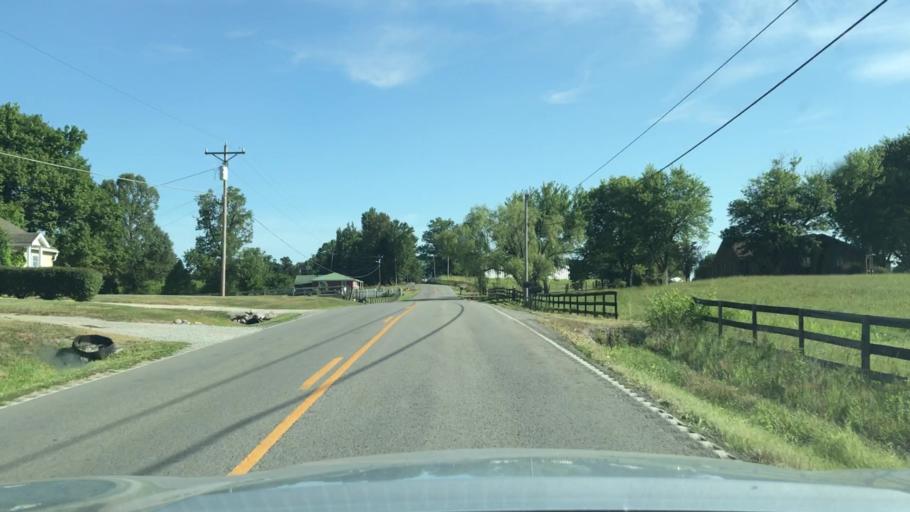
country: US
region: Kentucky
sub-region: Muhlenberg County
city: Greenville
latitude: 37.1579
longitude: -87.1420
